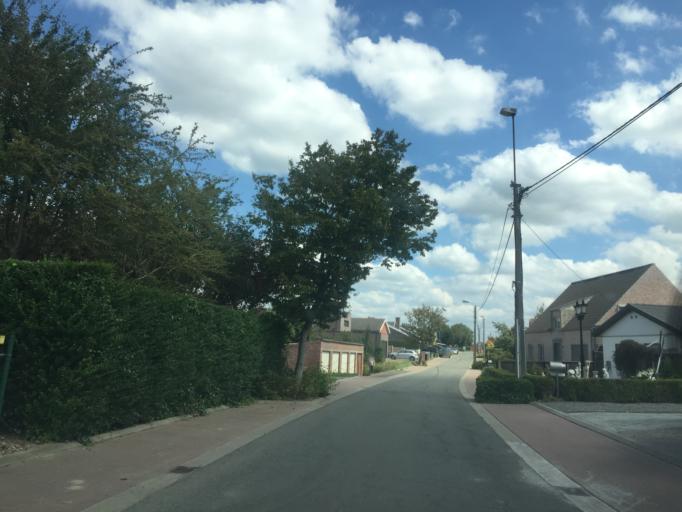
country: BE
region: Flanders
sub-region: Provincie West-Vlaanderen
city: Staden
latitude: 50.9728
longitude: 3.0252
